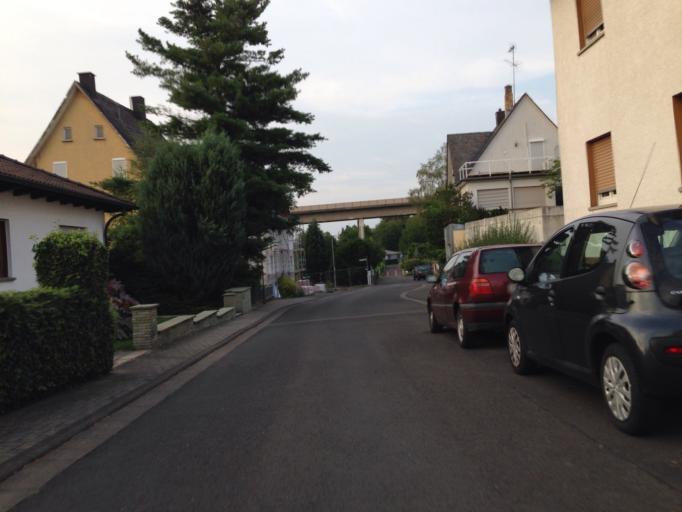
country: DE
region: Hesse
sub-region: Regierungsbezirk Giessen
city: Heuchelheim
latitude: 50.5647
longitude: 8.6494
